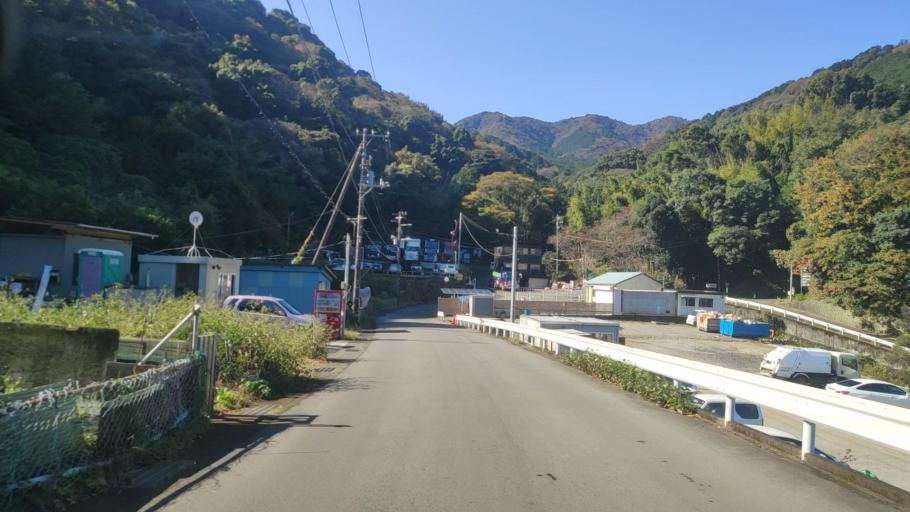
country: JP
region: Shizuoka
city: Atami
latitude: 35.0467
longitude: 139.0610
